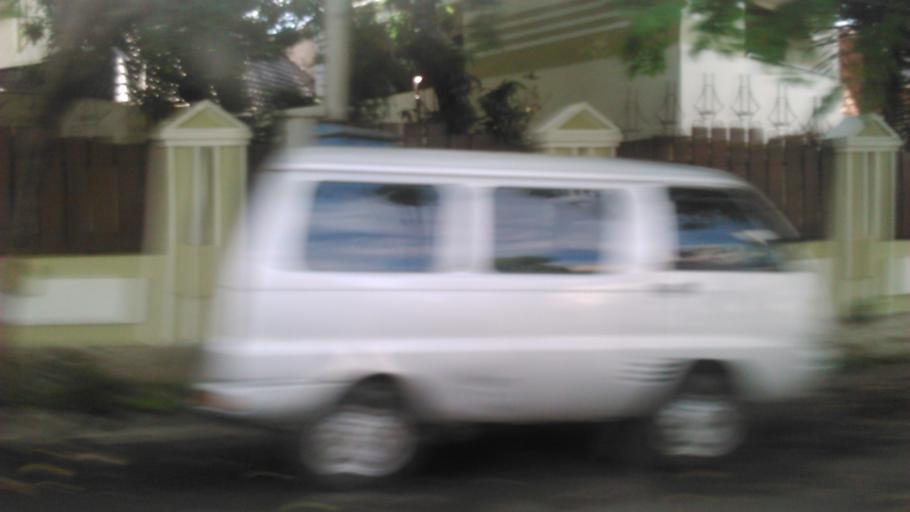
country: ID
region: East Java
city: Pacarkeling
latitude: -7.2579
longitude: 112.7542
